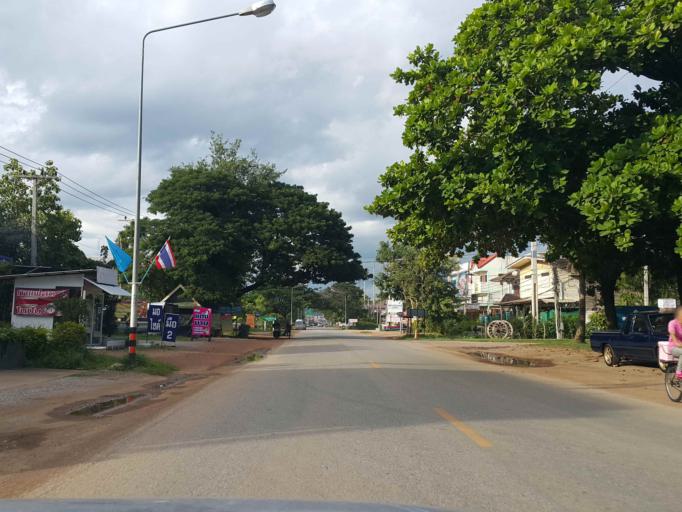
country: TH
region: Sukhothai
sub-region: Amphoe Si Satchanalai
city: Si Satchanalai
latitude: 17.5114
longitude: 99.7593
